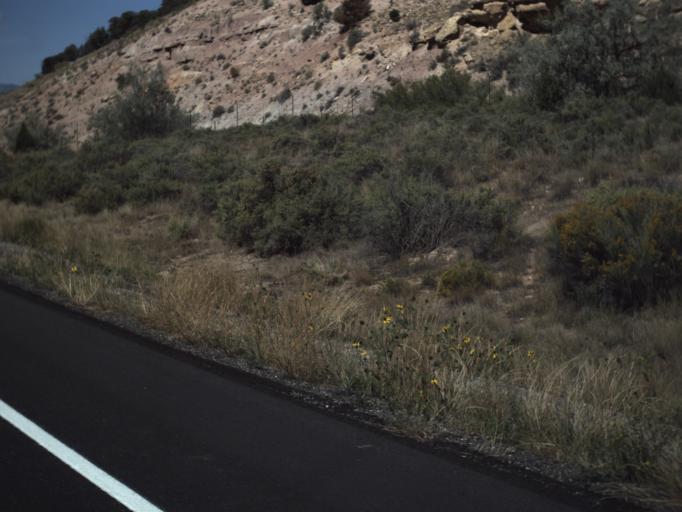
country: US
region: Utah
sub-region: Sevier County
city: Salina
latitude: 38.9161
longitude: -111.7360
